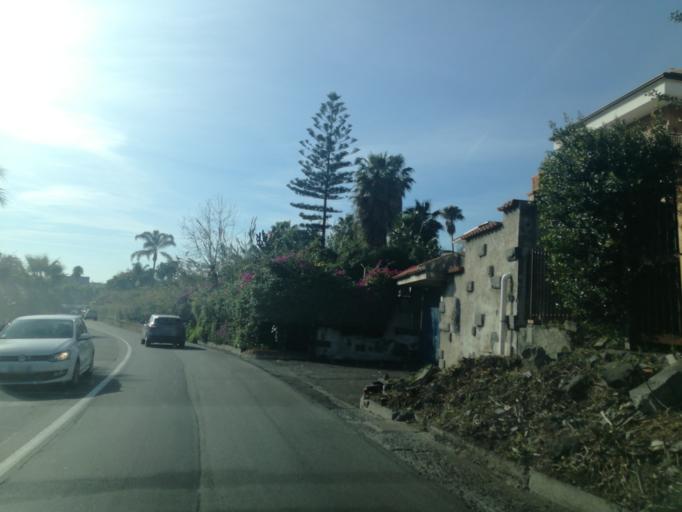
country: IT
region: Sicily
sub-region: Catania
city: Acitrezza
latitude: 37.5618
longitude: 15.1579
